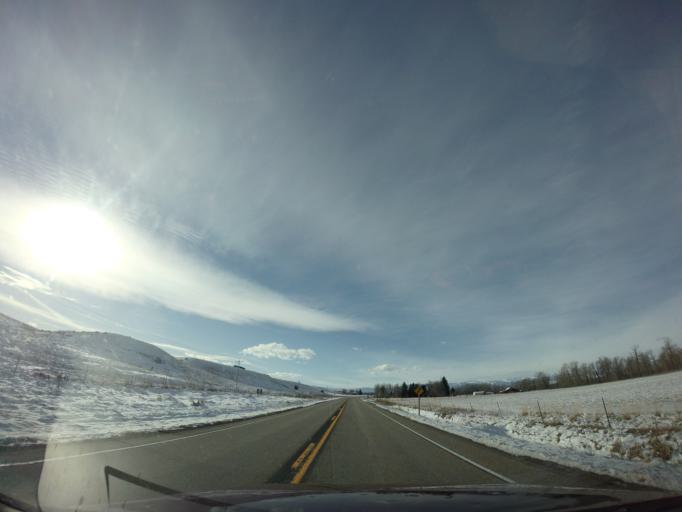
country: US
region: Montana
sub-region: Carbon County
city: Red Lodge
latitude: 45.3865
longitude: -109.1364
